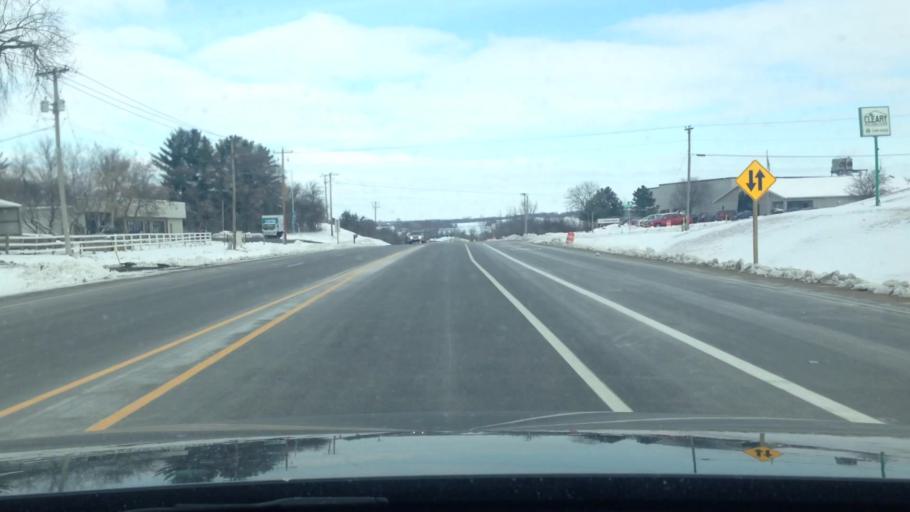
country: US
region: Wisconsin
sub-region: Walworth County
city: Lake Geneva
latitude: 42.6149
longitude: -88.4154
